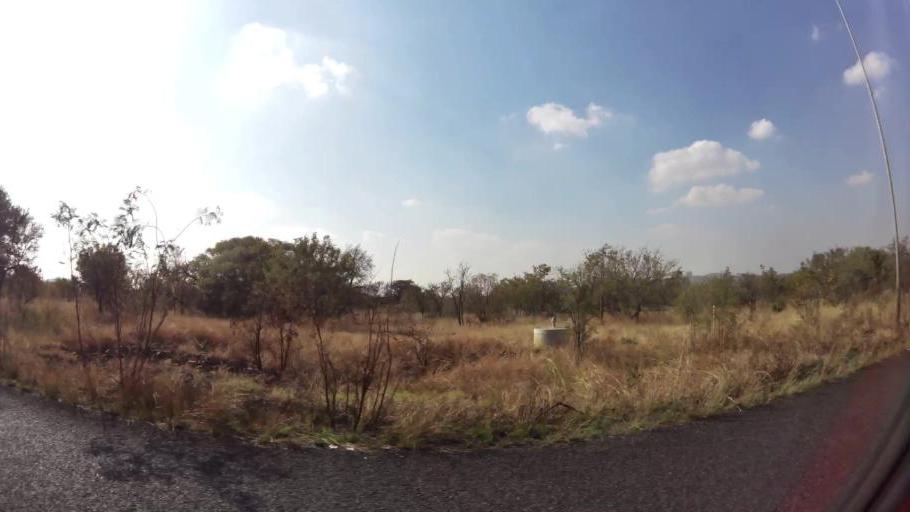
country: ZA
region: North-West
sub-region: Bojanala Platinum District Municipality
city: Rustenburg
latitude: -25.6059
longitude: 27.1416
